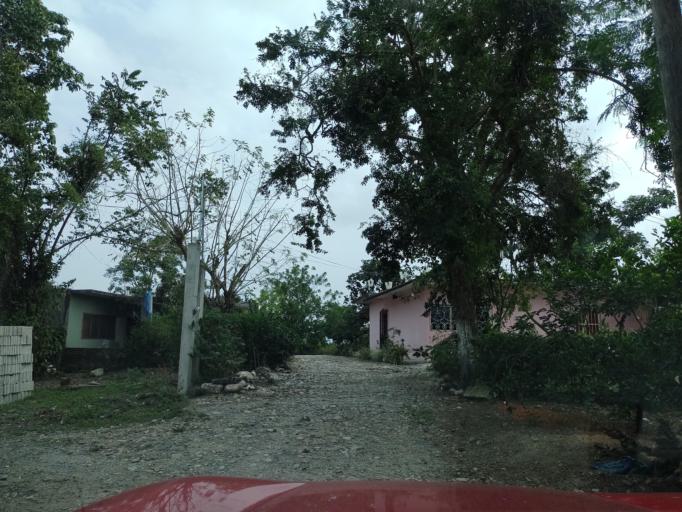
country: MX
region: Veracruz
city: Agua Dulce
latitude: 20.3425
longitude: -97.2893
